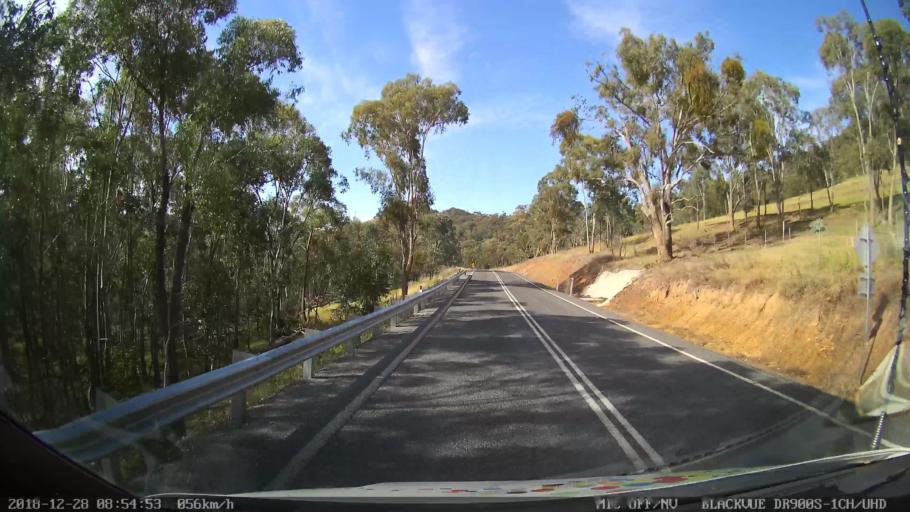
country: AU
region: New South Wales
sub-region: Upper Lachlan Shire
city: Crookwell
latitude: -34.0957
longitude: 149.3325
